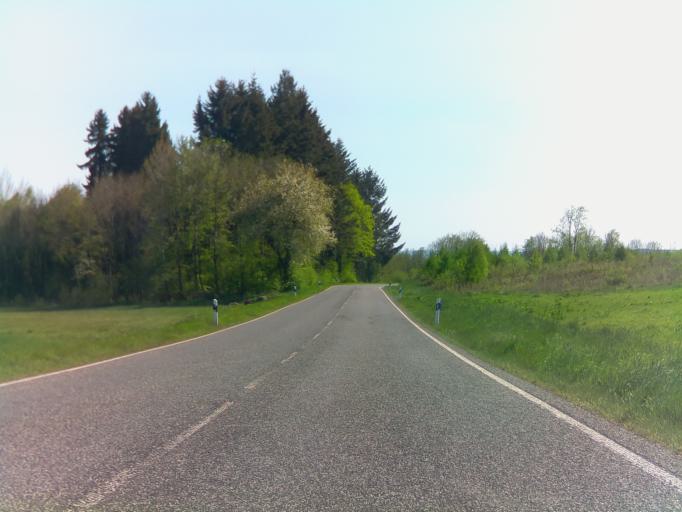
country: DE
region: Hesse
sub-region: Regierungsbezirk Darmstadt
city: Birstein
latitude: 50.4065
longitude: 9.3180
